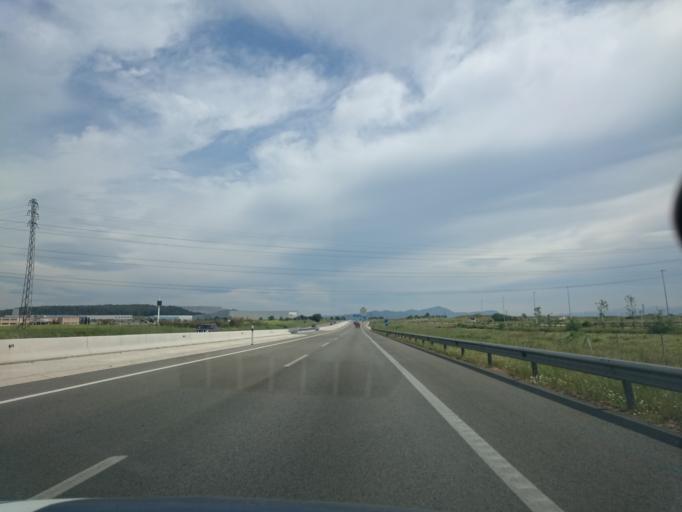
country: ES
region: Catalonia
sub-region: Provincia de Barcelona
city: Sant Fruitos de Bages
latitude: 41.7695
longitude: 1.8724
